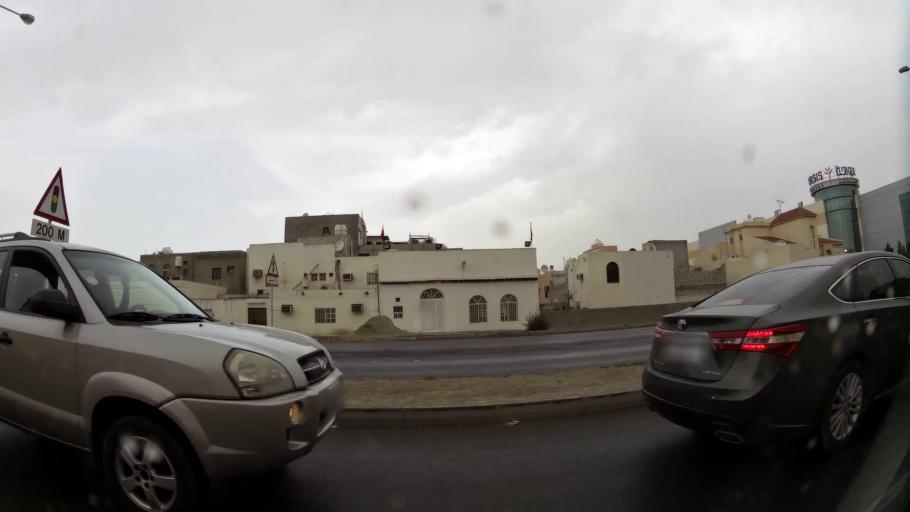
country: BH
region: Northern
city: Ar Rifa'
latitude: 26.1370
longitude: 50.5683
